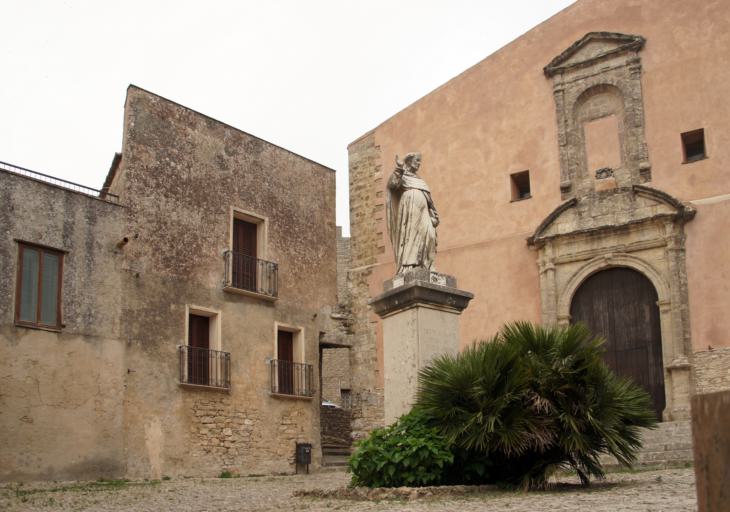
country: IT
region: Sicily
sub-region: Trapani
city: Erice
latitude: 38.0363
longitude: 12.5896
